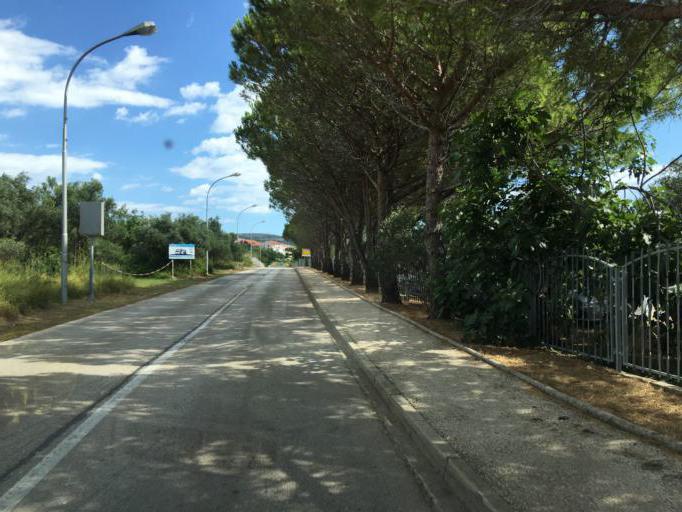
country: HR
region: Primorsko-Goranska
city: Punat
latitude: 45.0288
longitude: 14.6293
